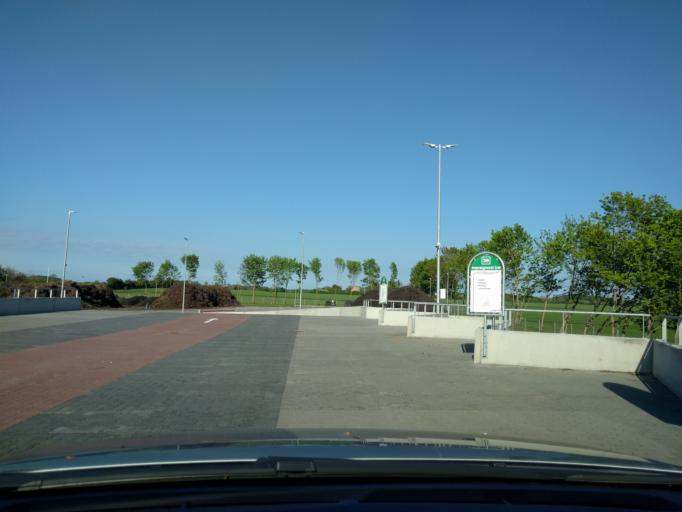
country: DK
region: South Denmark
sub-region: Kerteminde Kommune
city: Kerteminde
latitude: 55.4730
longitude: 10.6650
